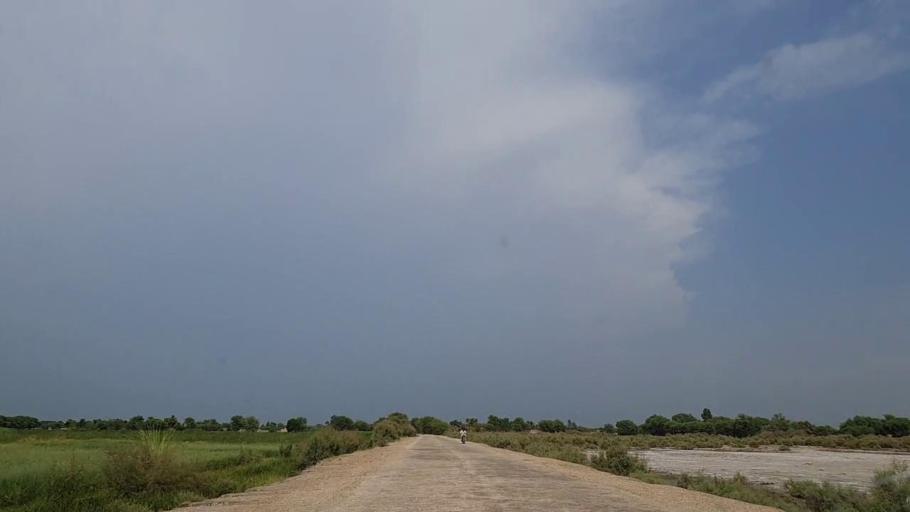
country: PK
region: Sindh
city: Khanpur
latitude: 27.8380
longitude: 69.4754
